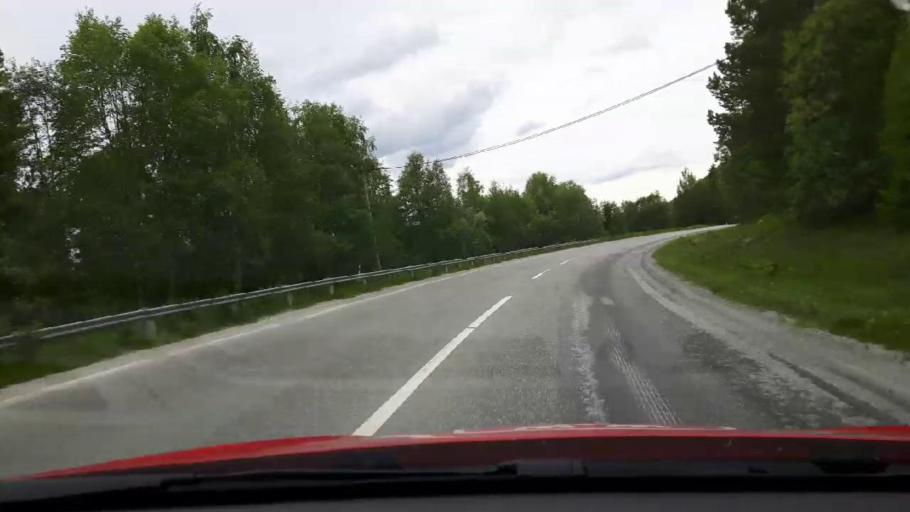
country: NO
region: Hedmark
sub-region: Engerdal
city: Engerdal
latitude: 62.5343
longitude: 12.5595
